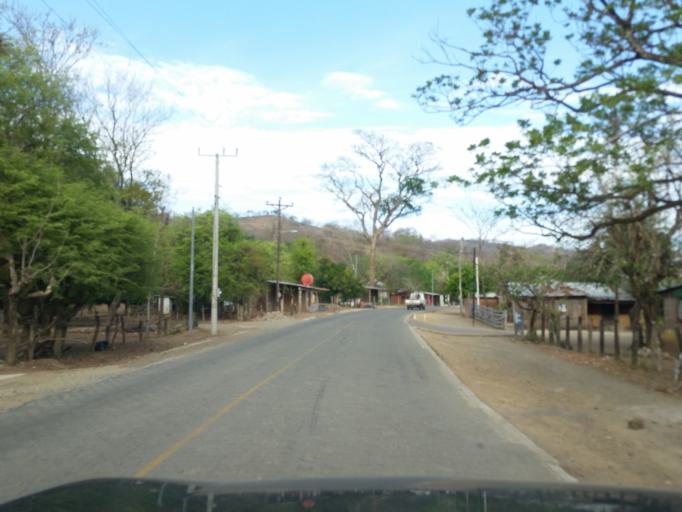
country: NI
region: Rivas
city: Tola
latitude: 11.3939
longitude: -85.9665
